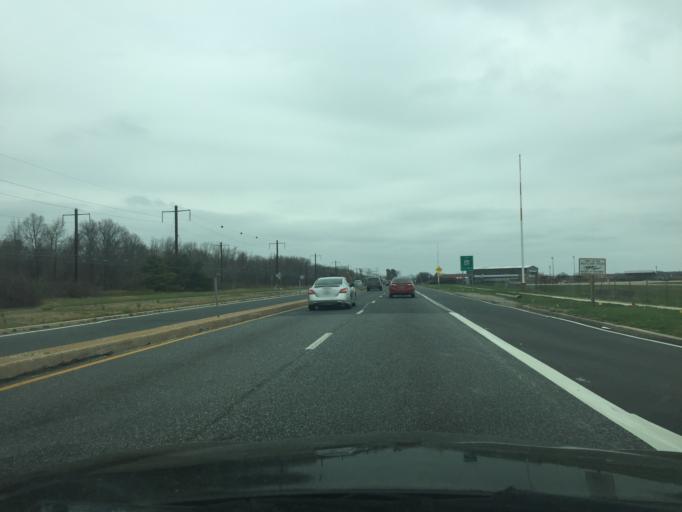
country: US
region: Maryland
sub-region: Baltimore County
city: Middle River
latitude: 39.3354
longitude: -76.4283
